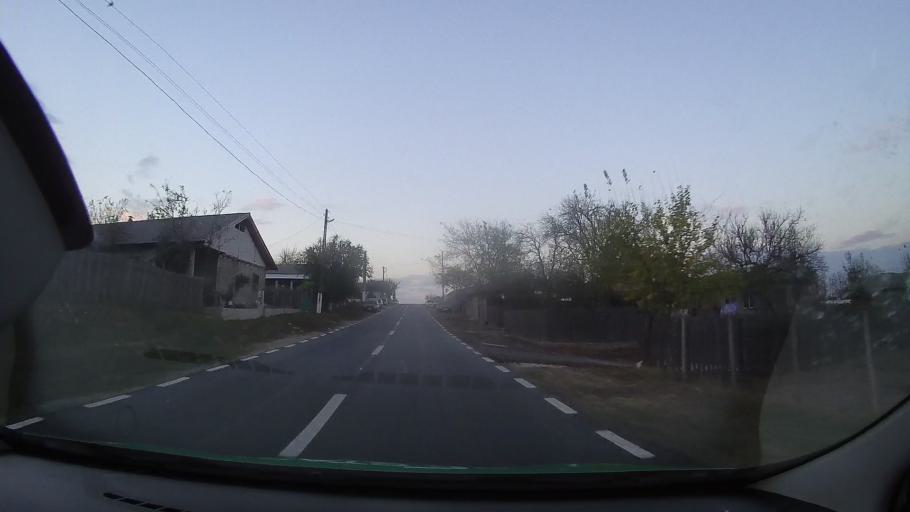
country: RO
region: Constanta
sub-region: Comuna Baneasa
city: Baneasa
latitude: 44.1014
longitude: 27.6759
